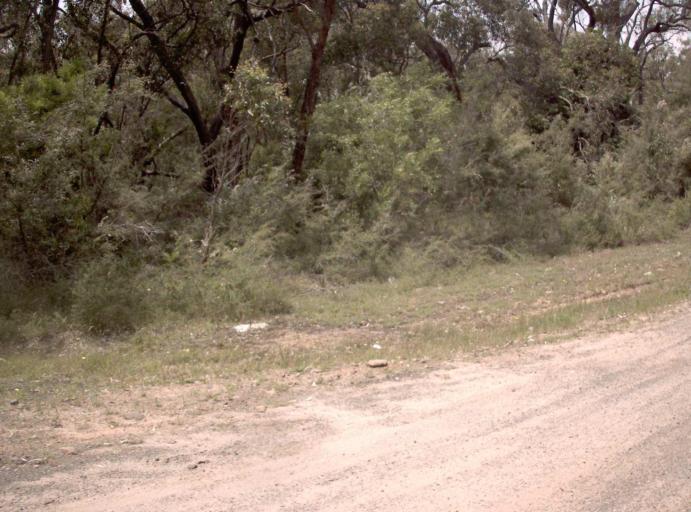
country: AU
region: Victoria
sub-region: Latrobe
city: Traralgon
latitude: -38.3145
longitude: 146.7190
